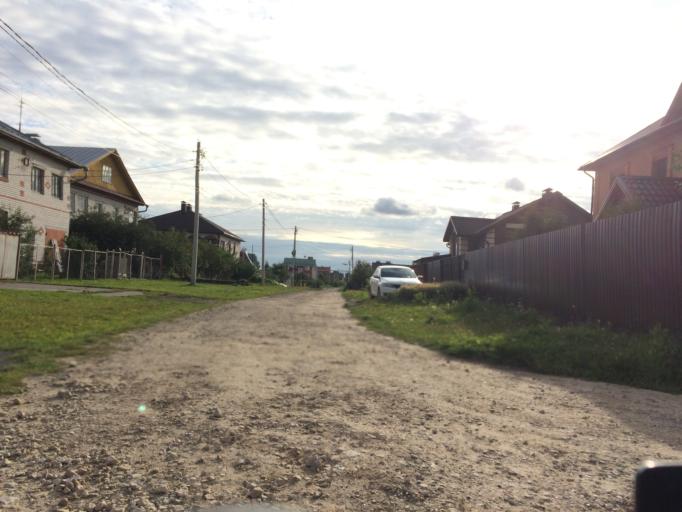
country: RU
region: Mariy-El
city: Yoshkar-Ola
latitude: 56.6541
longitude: 47.9921
